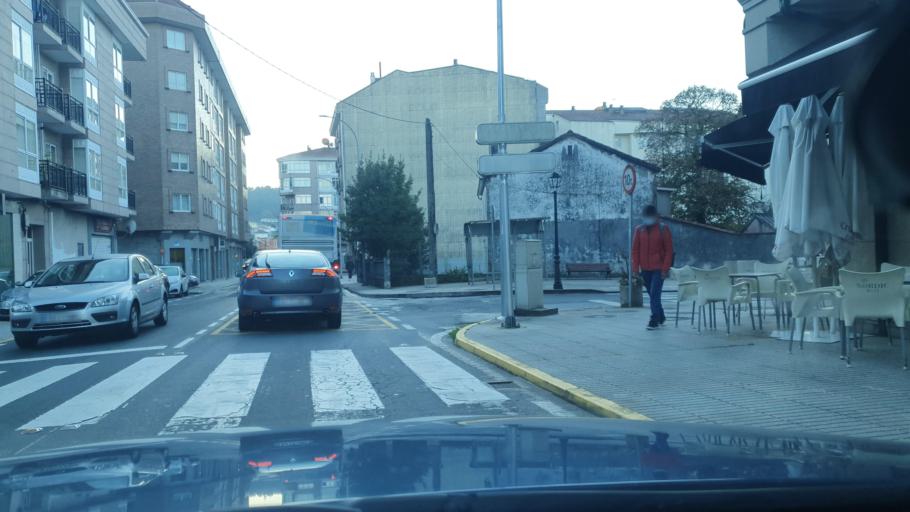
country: ES
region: Galicia
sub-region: Provincia da Coruna
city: Santiago de Compostela
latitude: 42.8427
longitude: -8.5800
